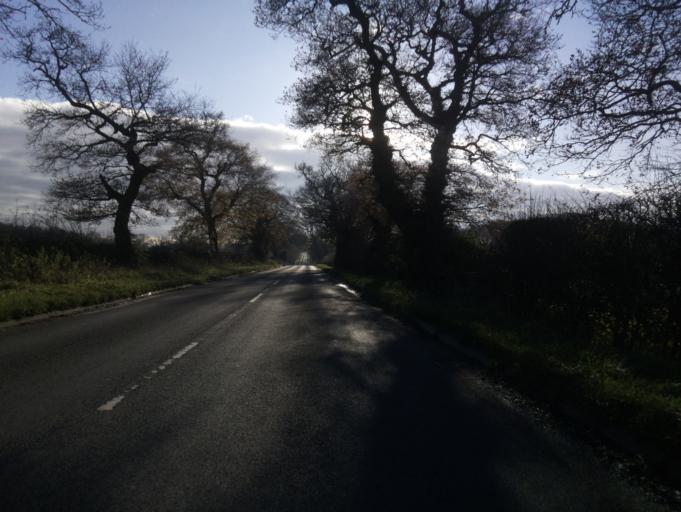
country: GB
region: England
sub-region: Staffordshire
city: Barton under Needwood
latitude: 52.8132
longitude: -1.7360
